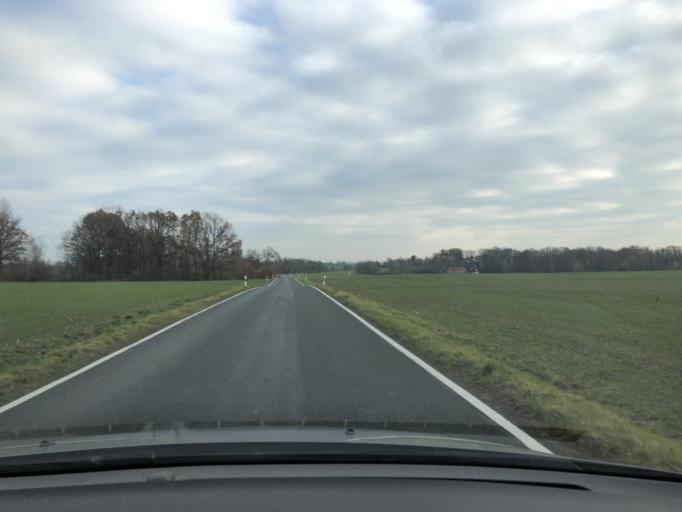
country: DE
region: Saxony
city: Mutzschen
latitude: 51.2828
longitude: 12.8689
